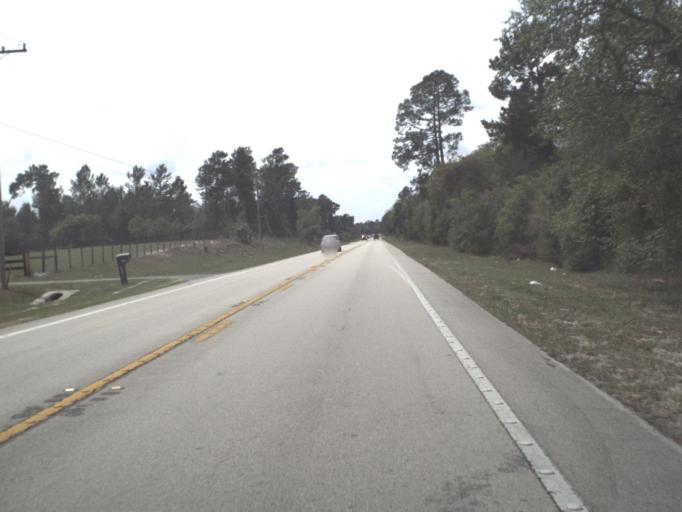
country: US
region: Florida
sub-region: Lake County
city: Lake Mack-Forest Hills
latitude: 28.9256
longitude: -81.4415
